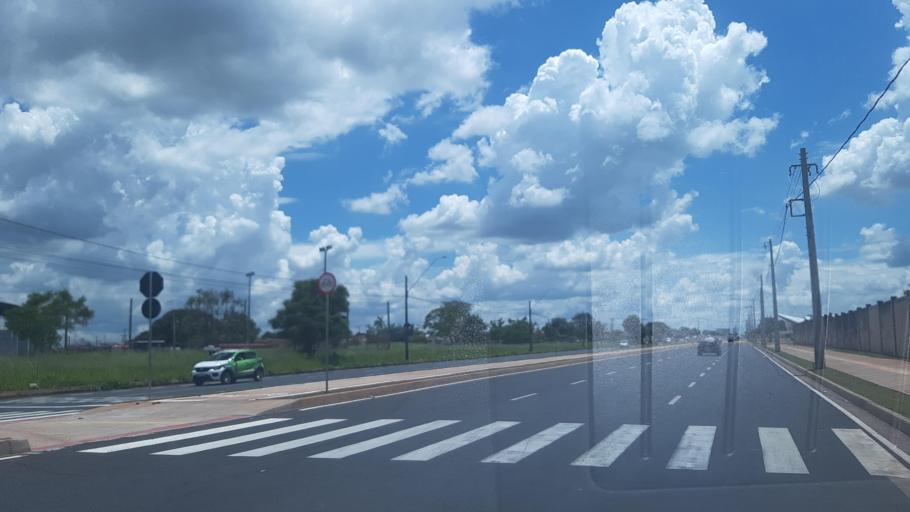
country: BR
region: Minas Gerais
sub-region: Uberlandia
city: Uberlandia
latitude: -18.9514
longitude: -48.3255
